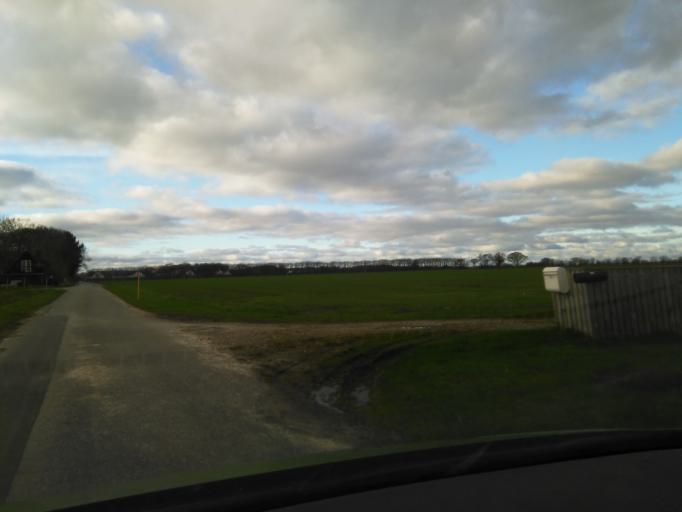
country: DK
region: Central Jutland
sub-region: Odder Kommune
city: Odder
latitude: 55.8722
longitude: 10.1778
